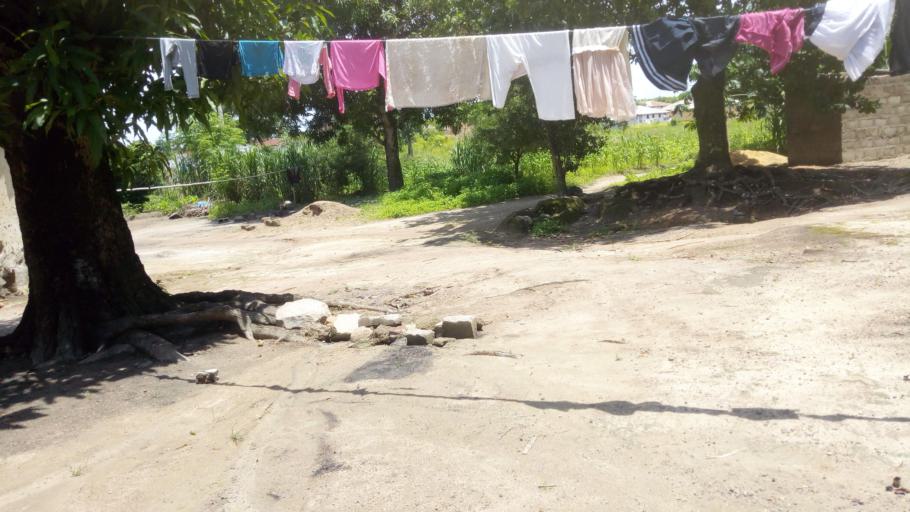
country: SL
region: Northern Province
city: Magburaka
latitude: 8.7141
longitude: -11.9607
